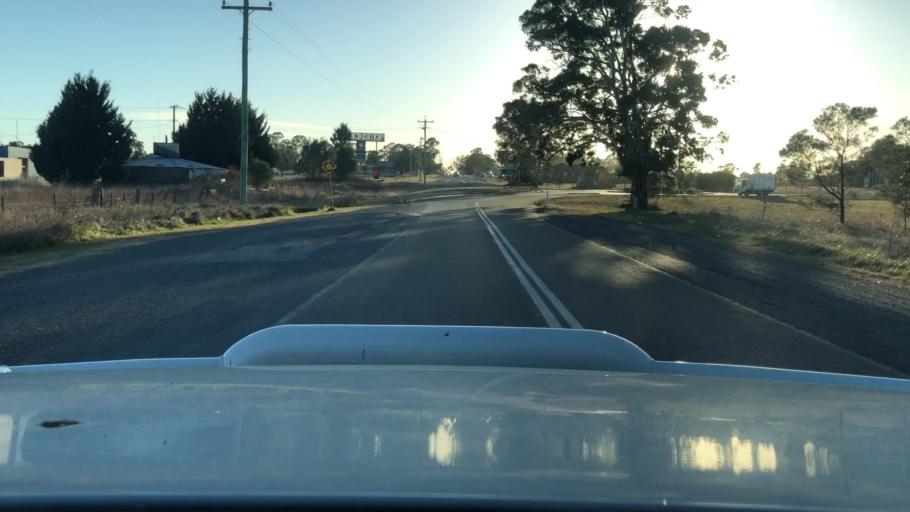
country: AU
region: New South Wales
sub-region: Goulburn Mulwaree
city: Goulburn
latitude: -34.7174
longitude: 149.9993
